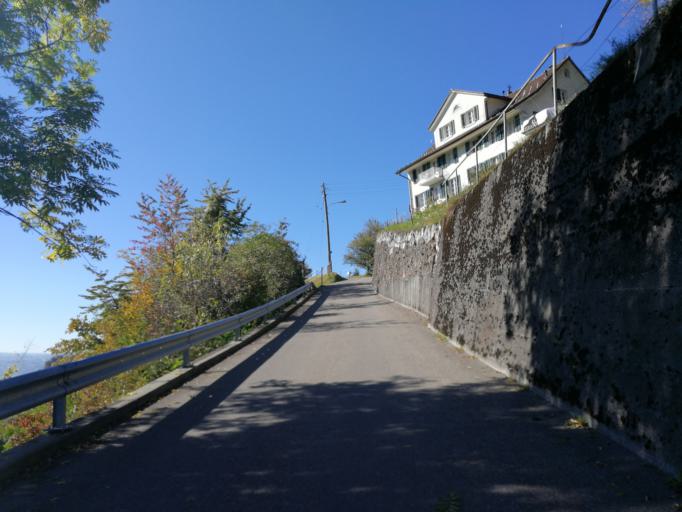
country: CH
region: Zurich
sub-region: Bezirk Hinwil
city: Wolfhausen
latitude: 47.2462
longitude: 8.7995
